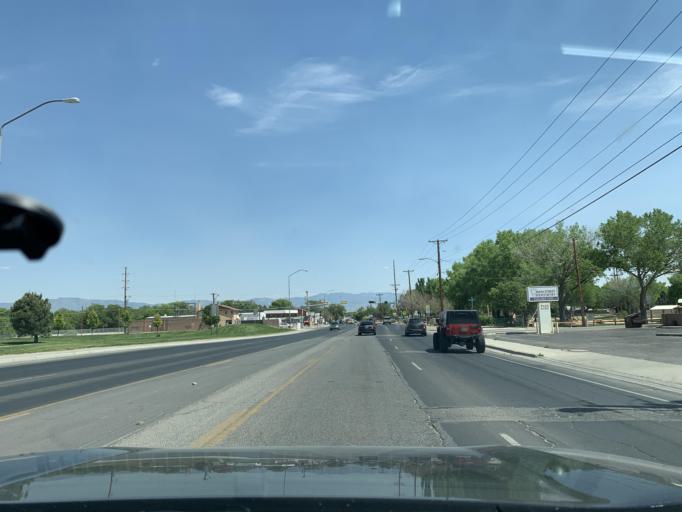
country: US
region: New Mexico
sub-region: Valencia County
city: Los Lunas
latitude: 34.8114
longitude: -106.7423
